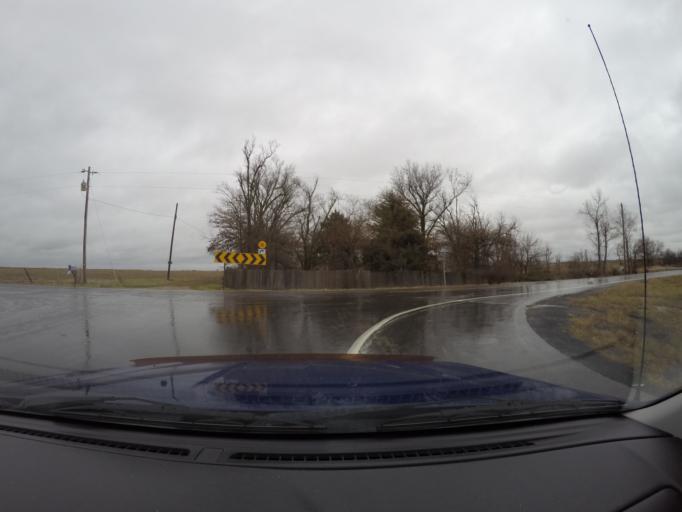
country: US
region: Kansas
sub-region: Jefferson County
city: Oskaloosa
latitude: 39.3401
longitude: -95.3295
